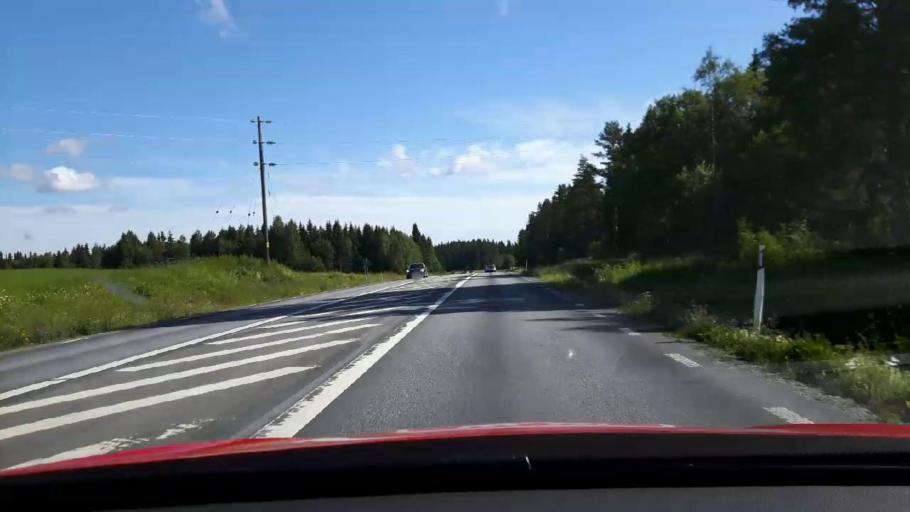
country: SE
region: Jaemtland
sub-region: OEstersunds Kommun
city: Lit
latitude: 63.2405
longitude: 14.7780
